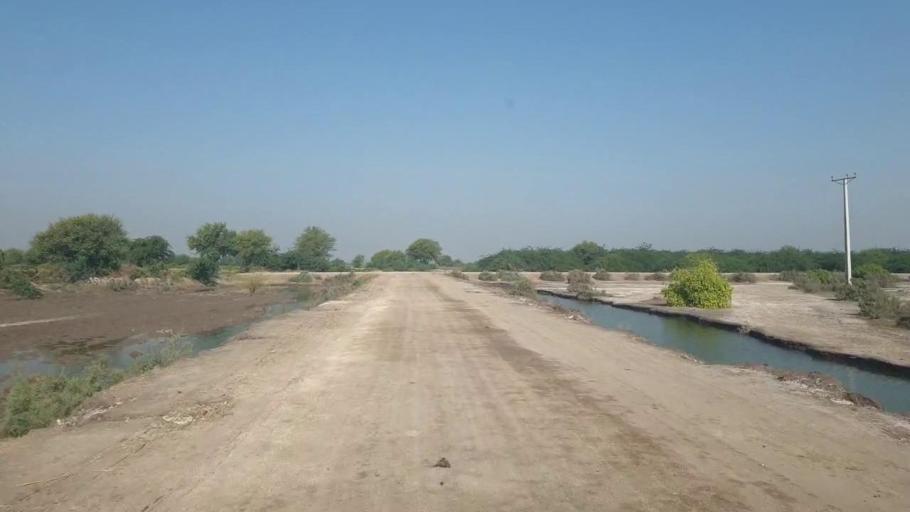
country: PK
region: Sindh
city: Tando Bago
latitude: 24.7378
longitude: 68.8886
